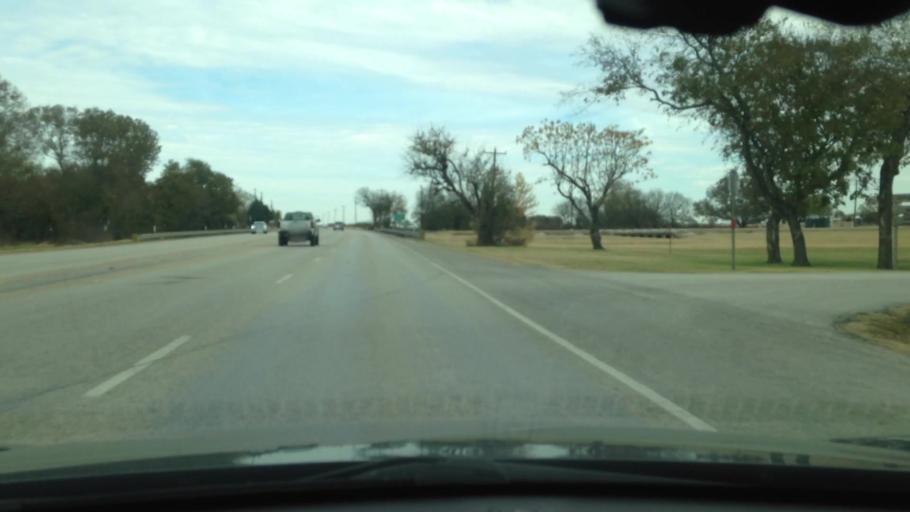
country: US
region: Texas
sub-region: Hays County
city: San Marcos
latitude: 29.8847
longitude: -97.8923
